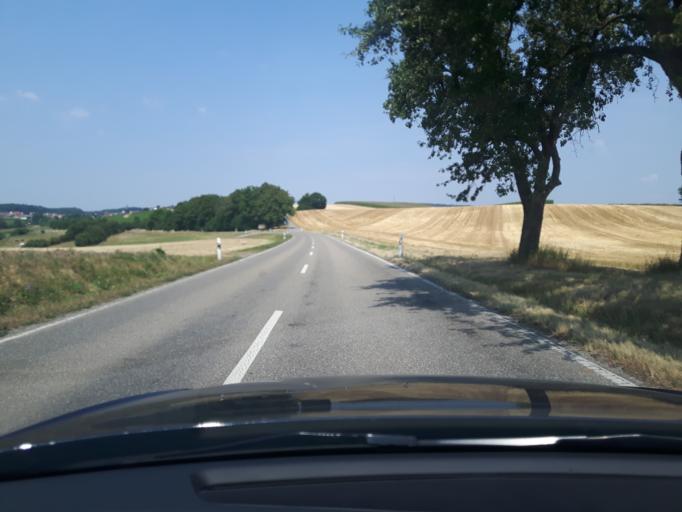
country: DE
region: Baden-Wuerttemberg
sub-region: Karlsruhe Region
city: Sulzfeld
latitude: 49.1670
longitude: 8.8564
